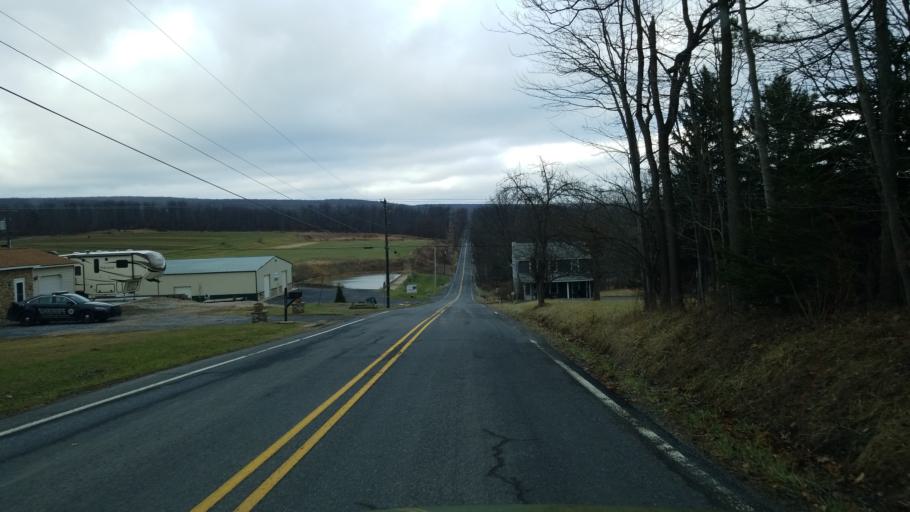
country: US
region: Pennsylvania
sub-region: Clearfield County
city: Hyde
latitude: 41.0420
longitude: -78.4892
